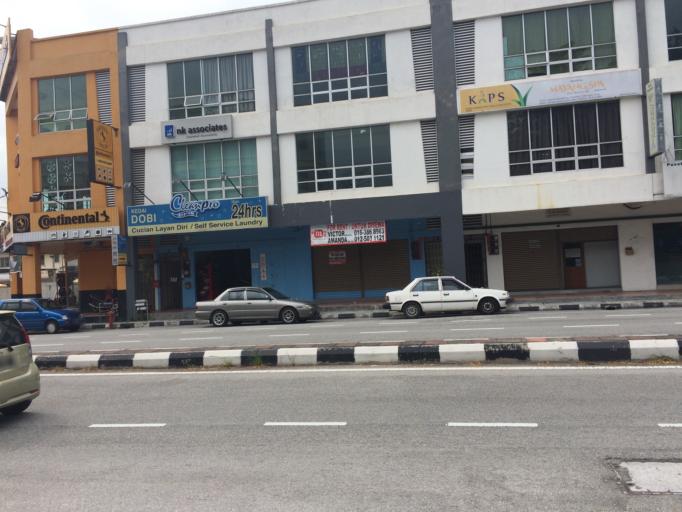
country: MY
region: Perak
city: Ipoh
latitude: 4.6053
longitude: 101.0932
